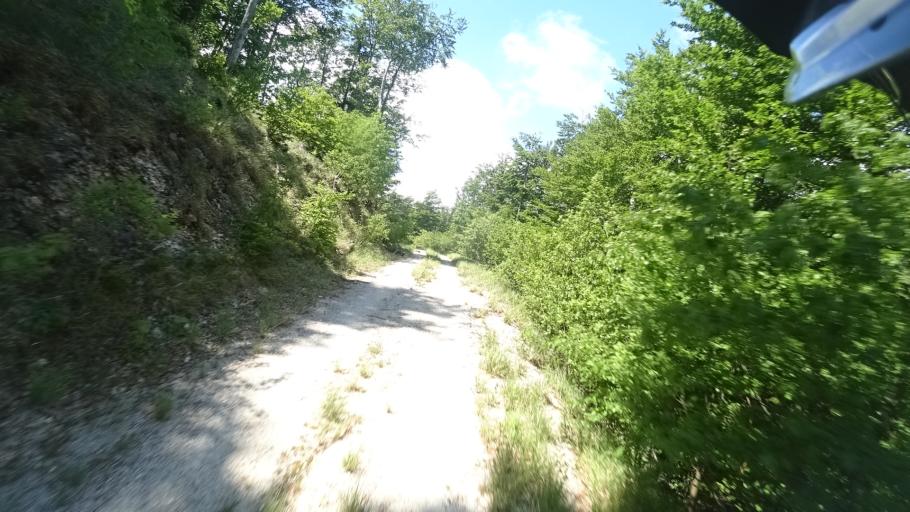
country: BA
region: Federation of Bosnia and Herzegovina
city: Orasac
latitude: 44.5708
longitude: 15.8539
